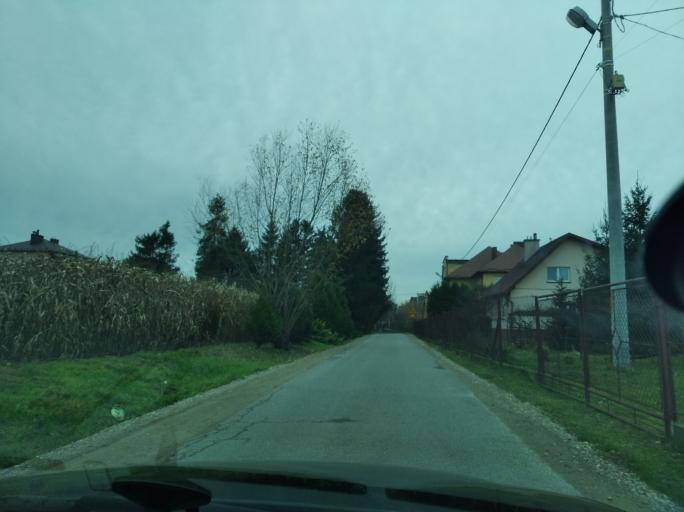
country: PL
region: Subcarpathian Voivodeship
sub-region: Powiat przeworski
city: Grzeska
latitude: 50.0746
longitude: 22.4555
